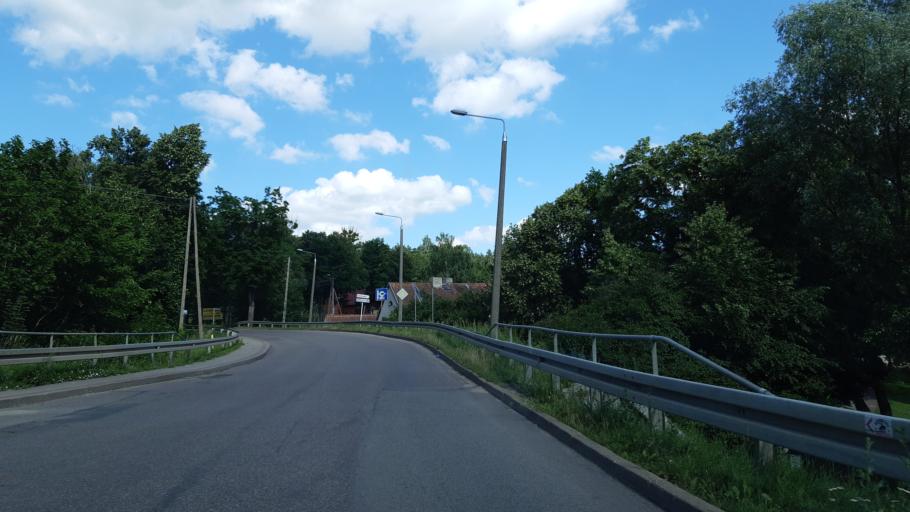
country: PL
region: Warmian-Masurian Voivodeship
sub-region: Powiat mragowski
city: Mragowo
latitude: 53.8761
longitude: 21.3139
